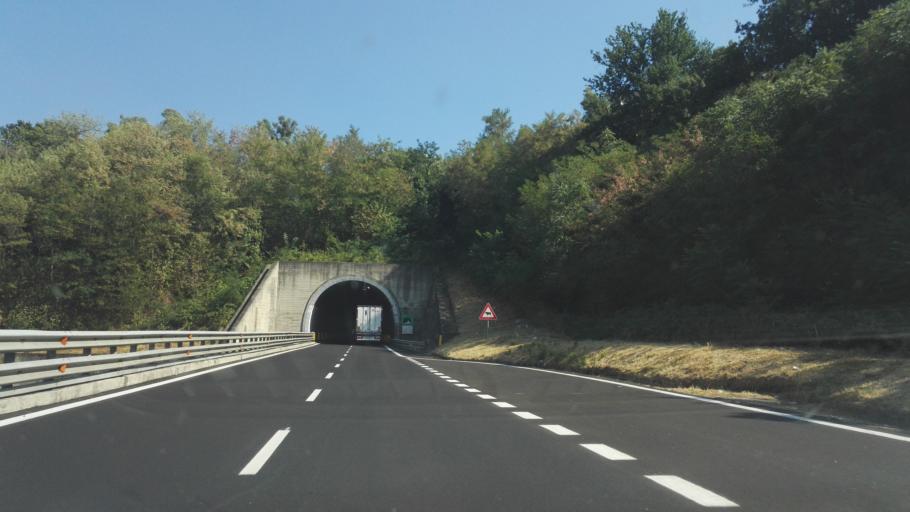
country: IT
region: Calabria
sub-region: Provincia di Cosenza
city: Laurignano
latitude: 39.2867
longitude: 16.2407
